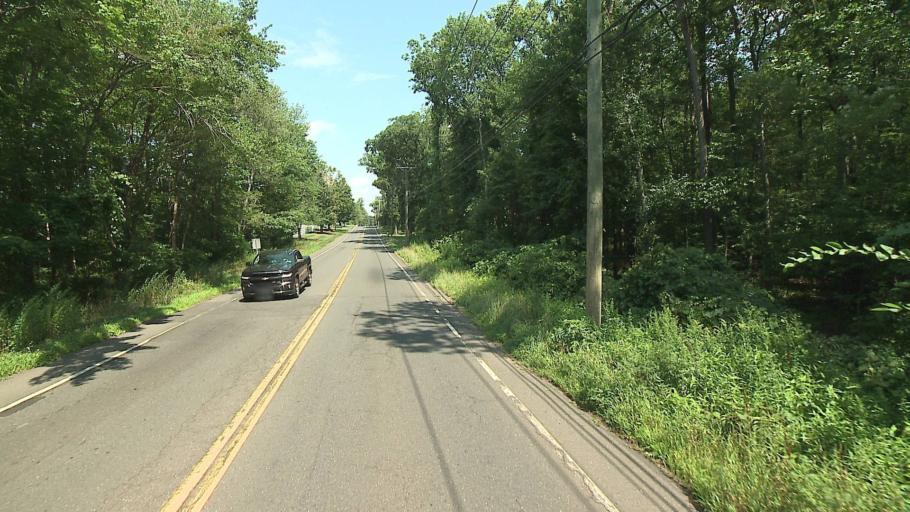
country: US
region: Connecticut
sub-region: Hartford County
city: Farmington
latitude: 41.7248
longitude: -72.8876
